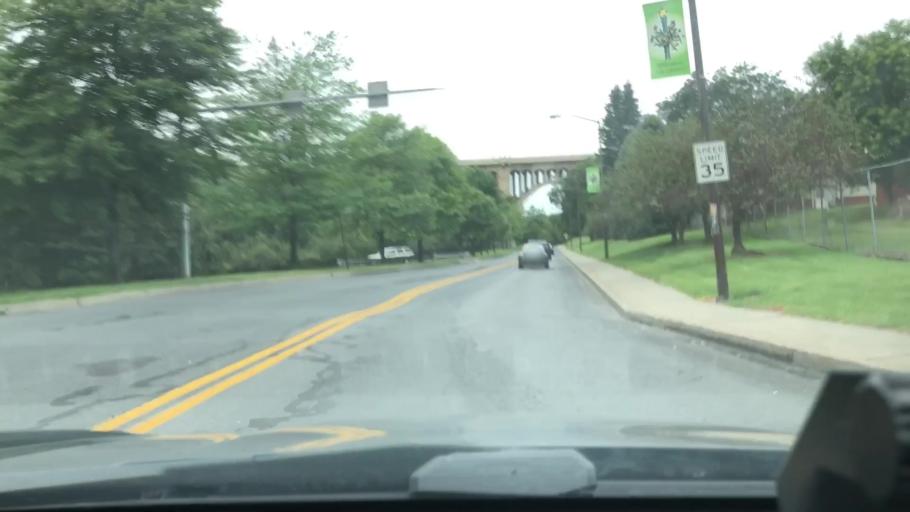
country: US
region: Pennsylvania
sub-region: Lehigh County
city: Allentown
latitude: 40.5975
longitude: -75.4682
